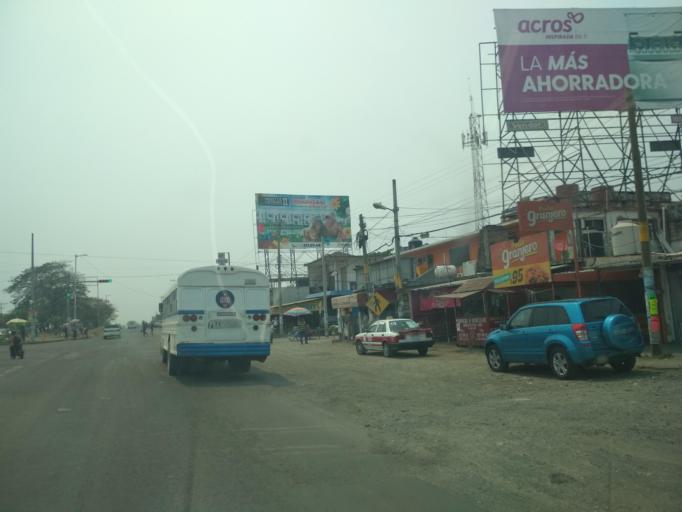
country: MX
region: Veracruz
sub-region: Veracruz
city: Lomas de Rio Medio Cuatro
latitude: 19.1681
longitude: -96.2221
